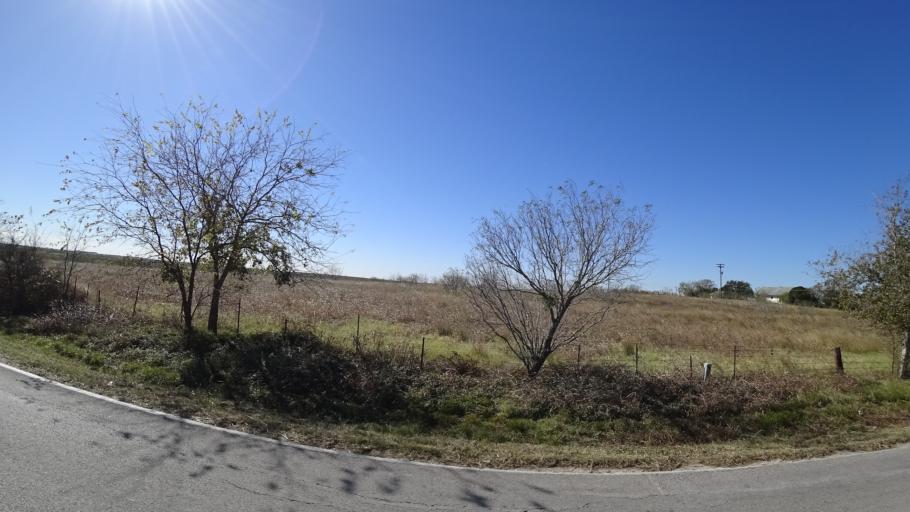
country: US
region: Texas
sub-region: Travis County
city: Garfield
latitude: 30.1273
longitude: -97.6008
